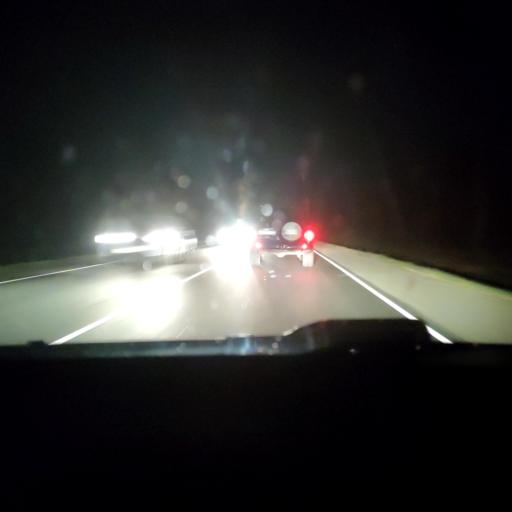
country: RU
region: Voronezj
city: Panino
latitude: 51.4750
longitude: 40.0143
